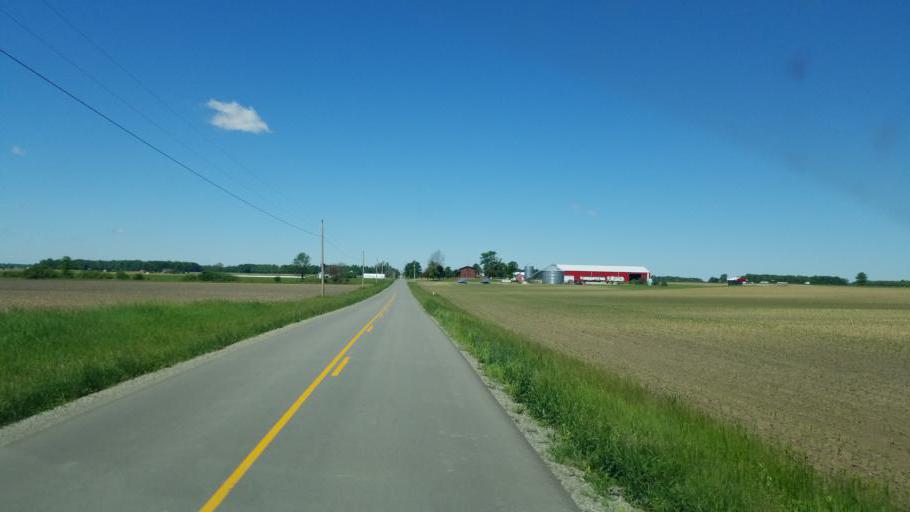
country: US
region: Ohio
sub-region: Shelby County
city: Jackson Center
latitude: 40.4174
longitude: -83.9767
